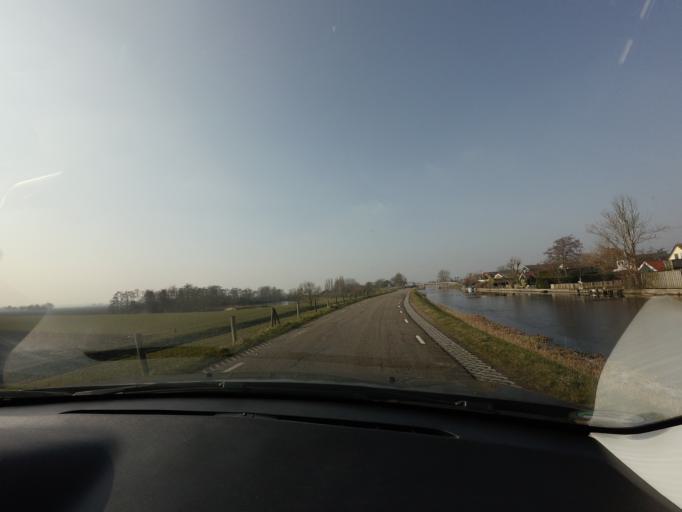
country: NL
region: North Holland
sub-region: Gemeente Heerhugowaard
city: Heerhugowaard
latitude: 52.6336
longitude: 4.8794
